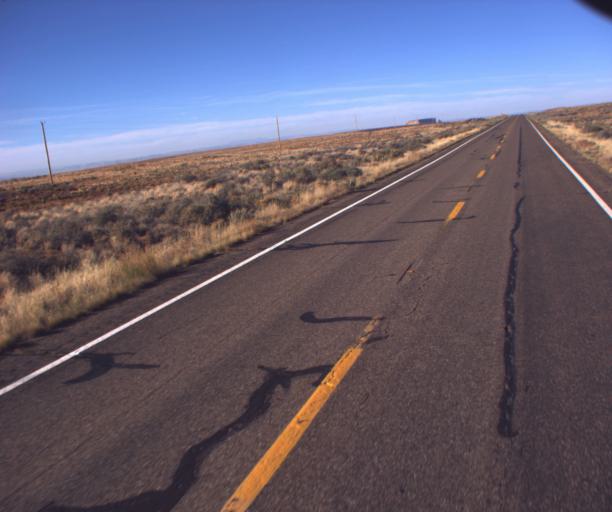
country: US
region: Arizona
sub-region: Coconino County
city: LeChee
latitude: 36.7478
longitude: -111.2848
